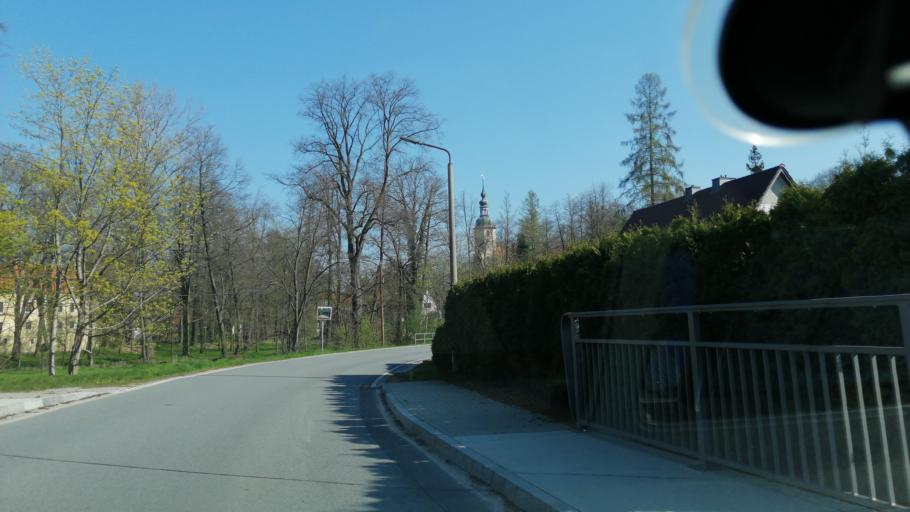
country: DE
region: Saxony
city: Goerlitz
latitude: 51.1784
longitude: 14.9341
